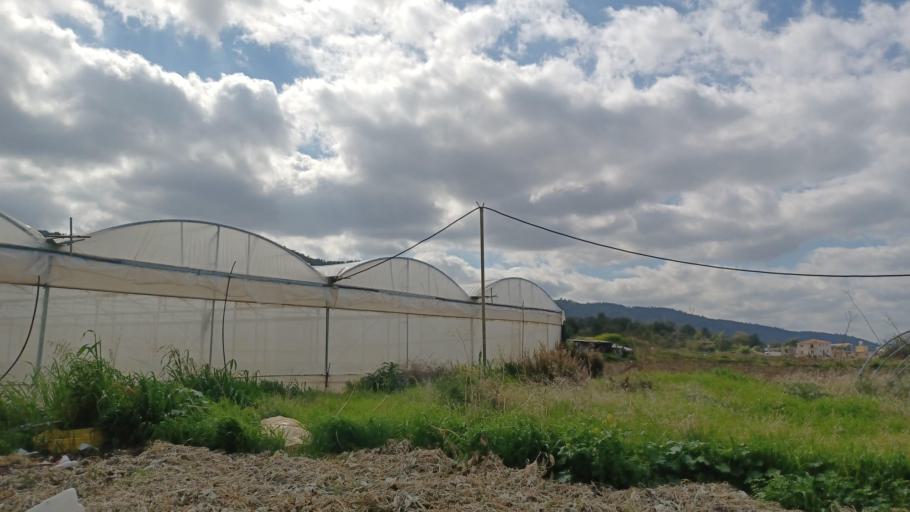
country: CY
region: Pafos
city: Polis
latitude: 35.1037
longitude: 32.5129
